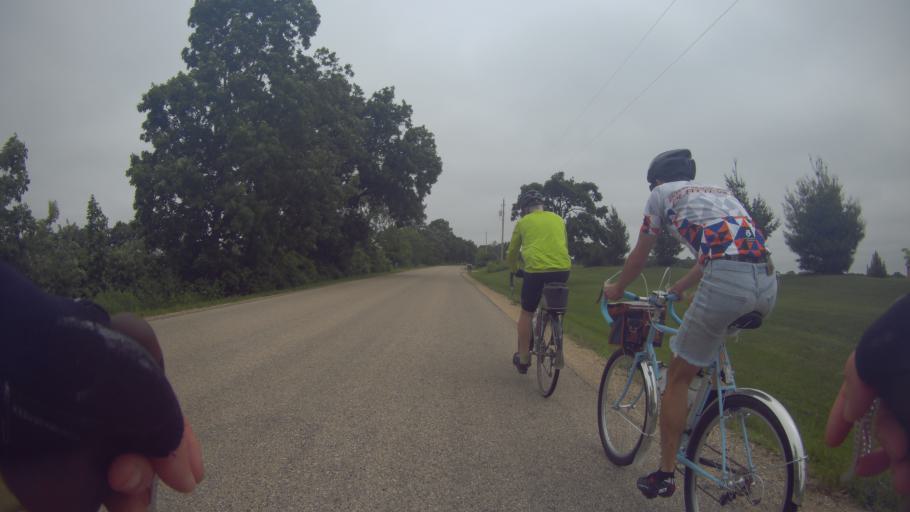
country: US
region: Wisconsin
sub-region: Green County
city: Brooklyn
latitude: 42.8623
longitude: -89.4135
